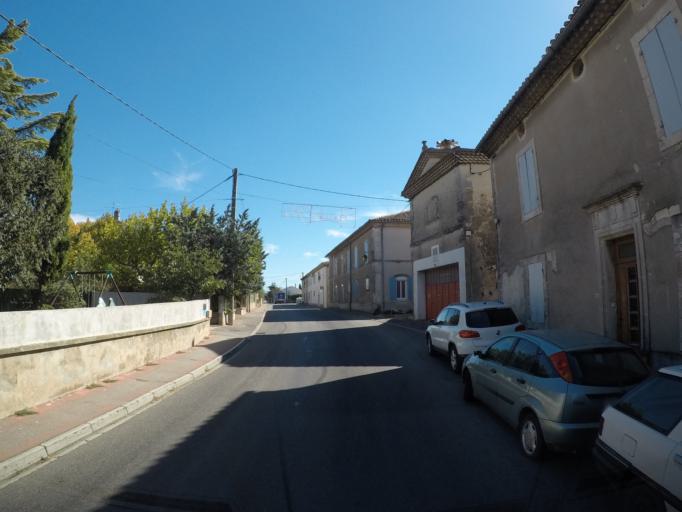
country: FR
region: Rhone-Alpes
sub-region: Departement de la Drome
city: Suze-la-Rousse
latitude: 44.2883
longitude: 4.8427
